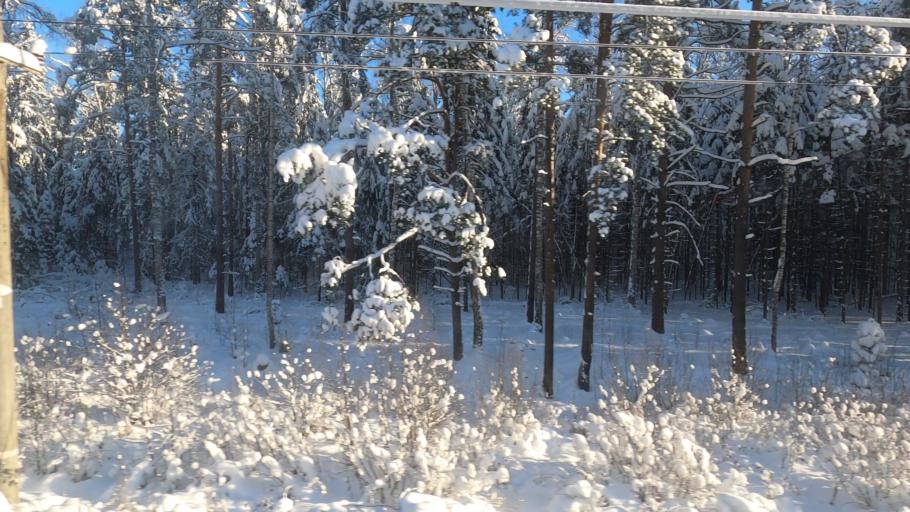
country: RU
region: Moskovskaya
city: Zhukovka
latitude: 56.5006
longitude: 37.5530
